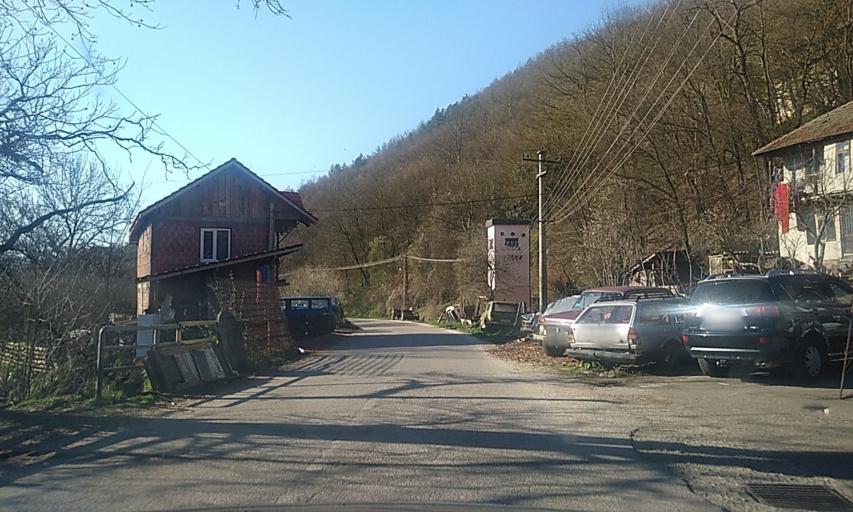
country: RS
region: Central Serbia
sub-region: Pcinjski Okrug
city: Bosilegrad
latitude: 42.4676
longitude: 22.4841
